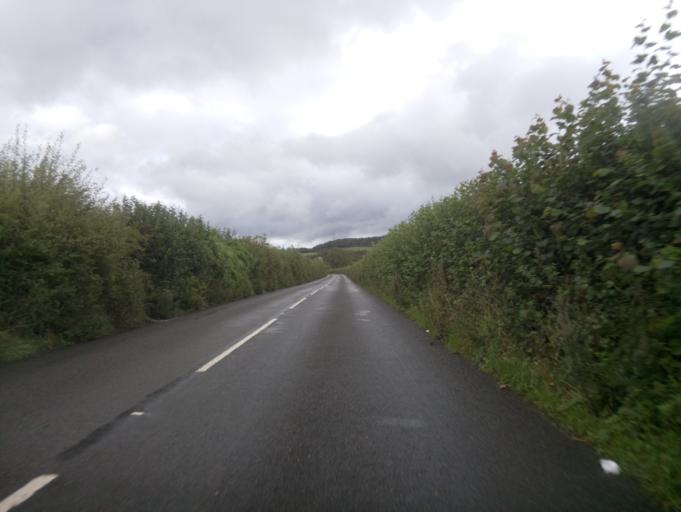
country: GB
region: England
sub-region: Devon
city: South Brent
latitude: 50.4274
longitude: -3.8217
